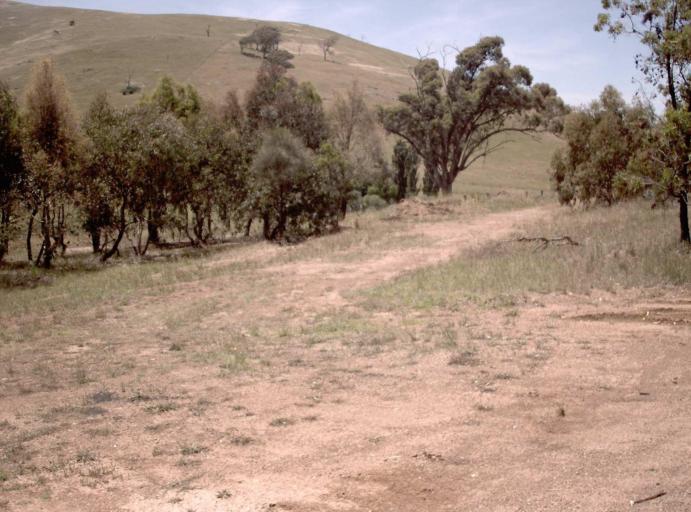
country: AU
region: Victoria
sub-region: East Gippsland
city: Bairnsdale
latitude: -37.3536
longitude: 147.8068
